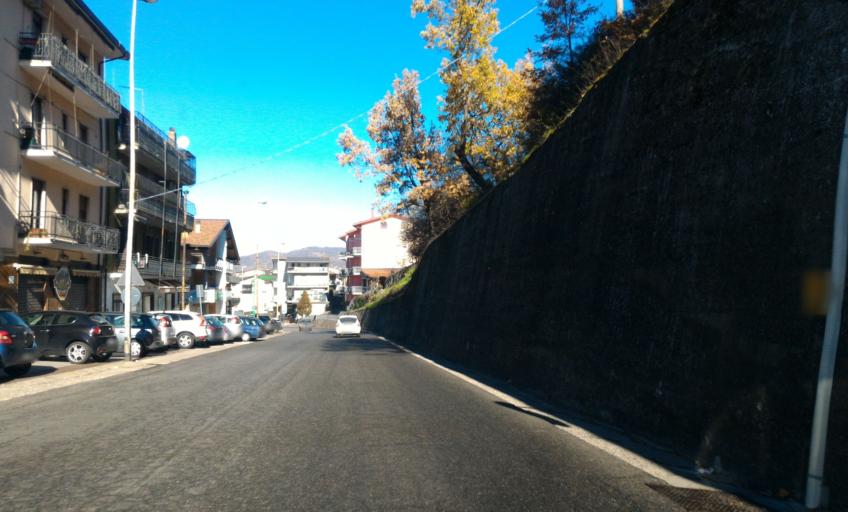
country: IT
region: Calabria
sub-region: Provincia di Cosenza
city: Spezzano della Sila
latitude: 39.3018
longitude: 16.3406
